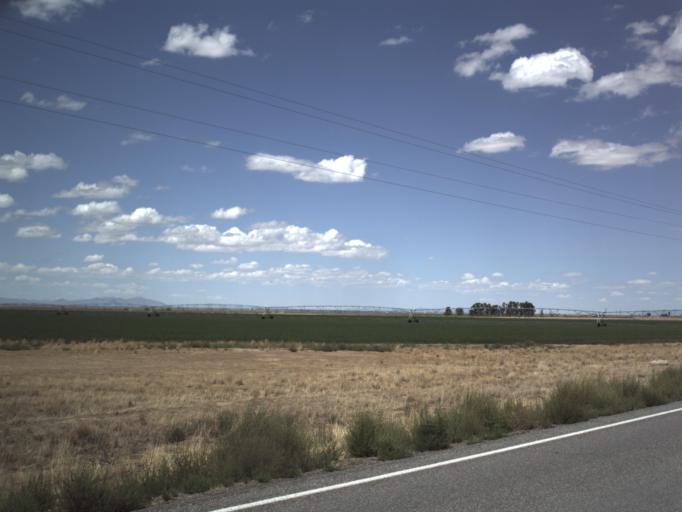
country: US
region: Utah
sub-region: Millard County
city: Delta
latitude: 39.1882
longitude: -112.4100
